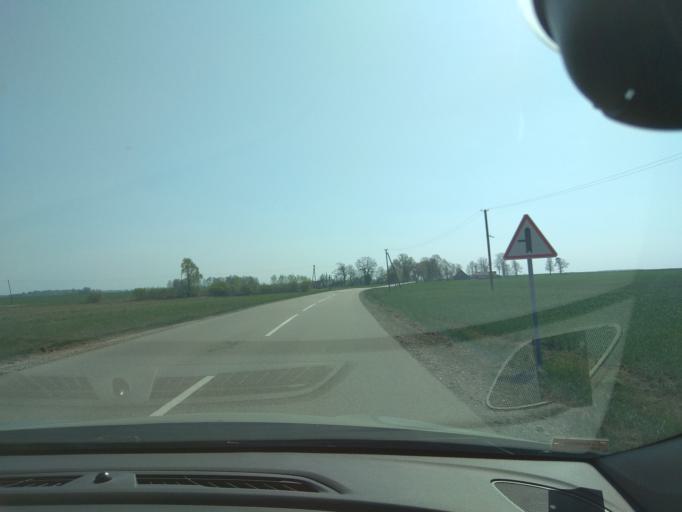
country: LT
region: Panevezys
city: Pasvalys
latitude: 55.9684
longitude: 24.2084
